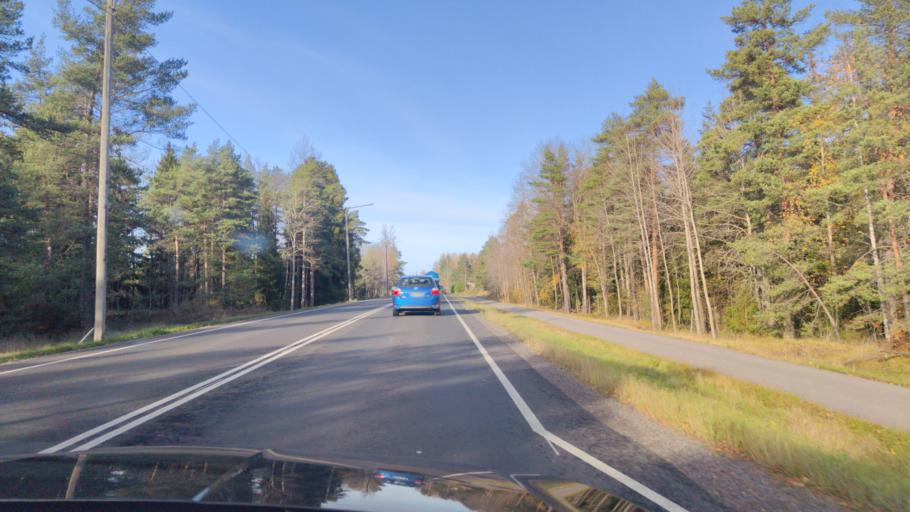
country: FI
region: Varsinais-Suomi
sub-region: Turku
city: Kaarina
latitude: 60.4489
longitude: 22.3733
